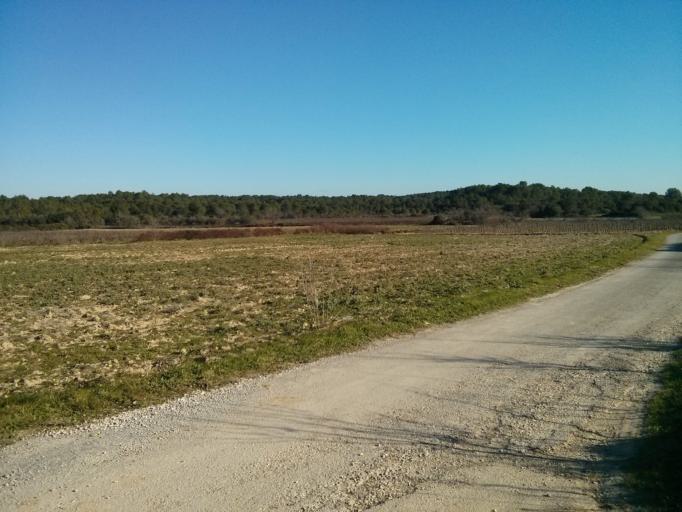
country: FR
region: Languedoc-Roussillon
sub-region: Departement du Gard
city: Aigues-Vives
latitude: 43.7533
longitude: 4.1765
